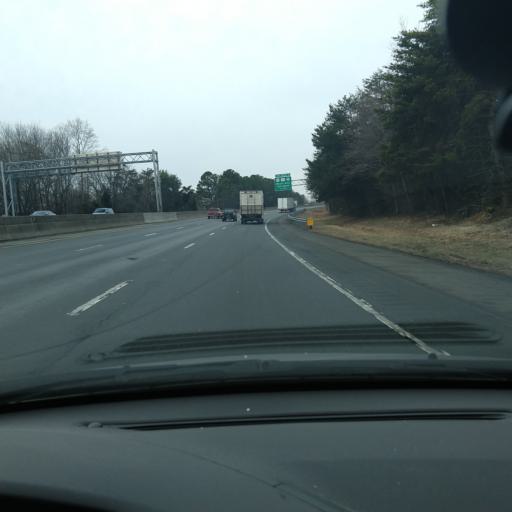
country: US
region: North Carolina
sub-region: Forsyth County
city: Winston-Salem
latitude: 36.0587
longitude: -80.2143
